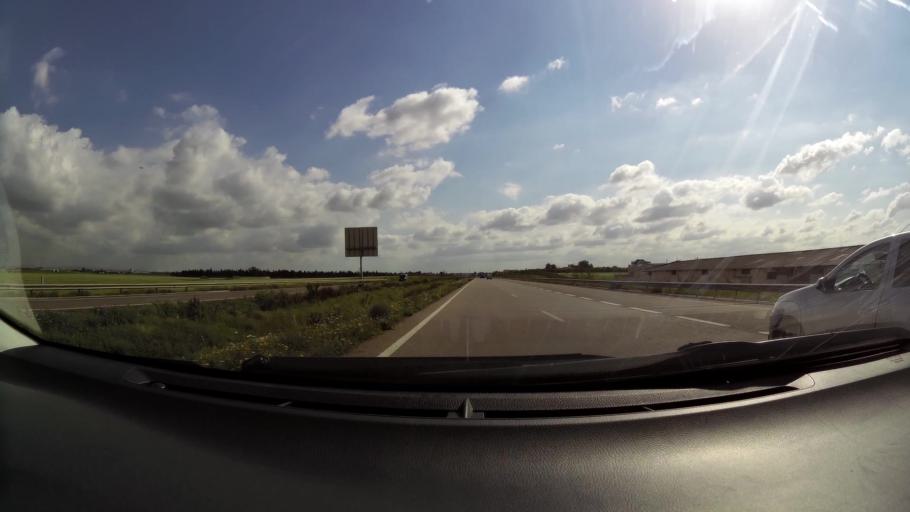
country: MA
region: Chaouia-Ouardigha
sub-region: Settat Province
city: Berrechid
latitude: 33.2664
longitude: -7.5515
